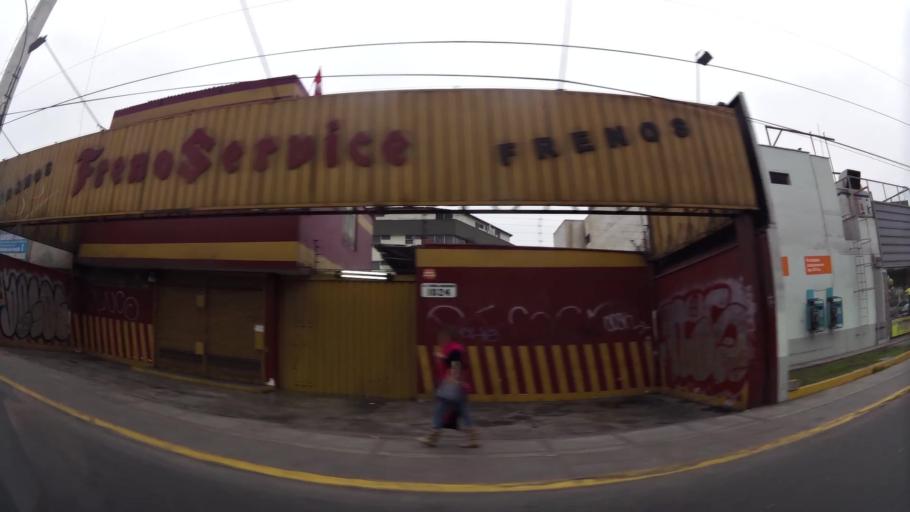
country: PE
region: Lima
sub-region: Lima
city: Surco
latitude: -12.1130
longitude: -77.0119
